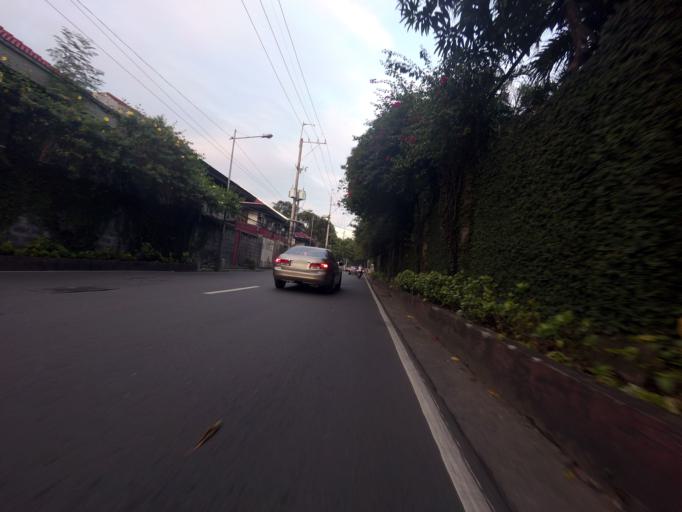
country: PH
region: Metro Manila
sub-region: San Juan
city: San Juan
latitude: 14.5963
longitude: 121.0313
